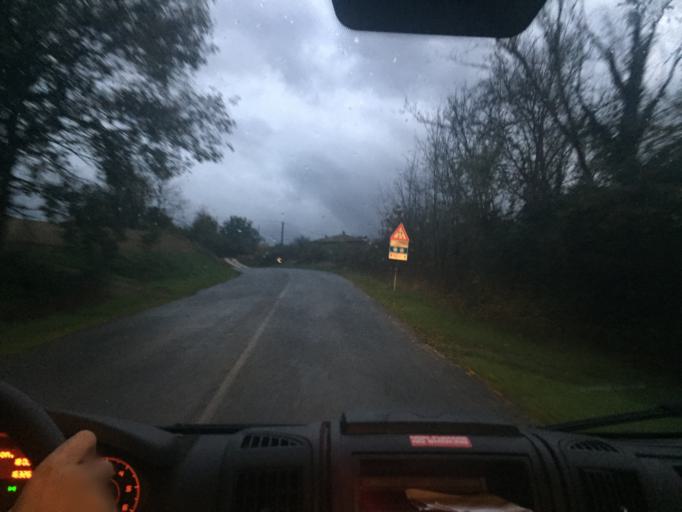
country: IT
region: The Marches
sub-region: Provincia di Macerata
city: Camerino
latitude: 43.1426
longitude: 13.0521
